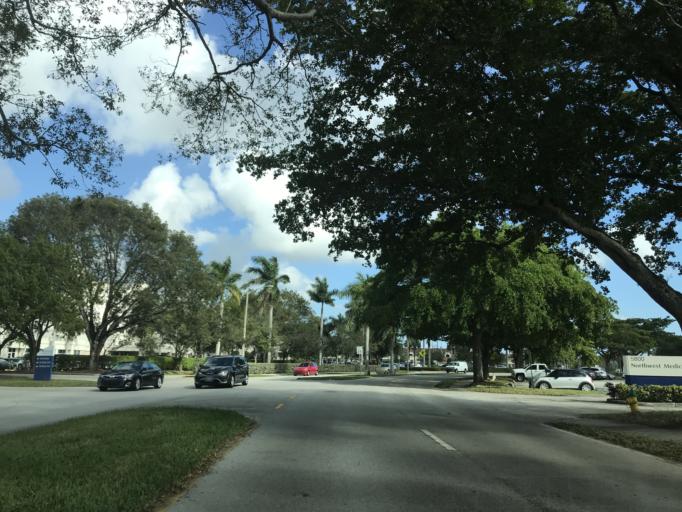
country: US
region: Florida
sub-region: Broward County
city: Margate
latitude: 26.2618
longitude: -80.2041
